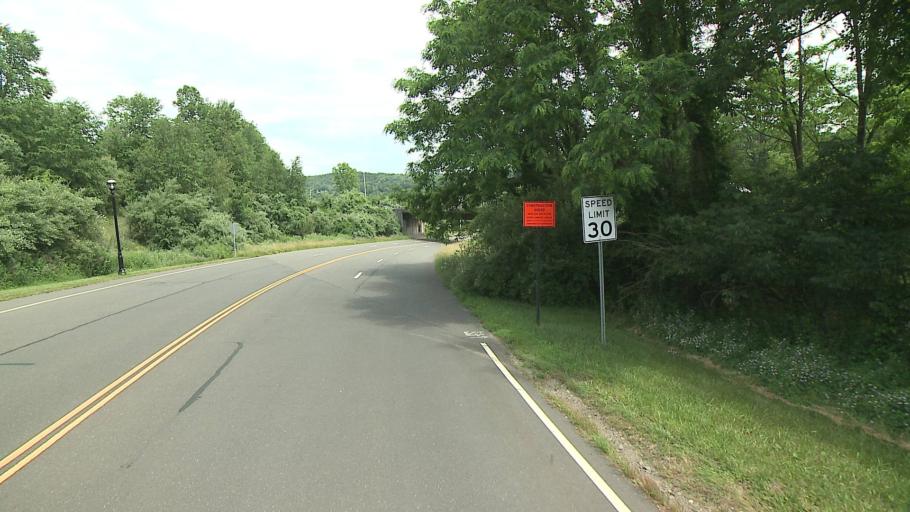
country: US
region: New York
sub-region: Putnam County
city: Peach Lake
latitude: 41.3890
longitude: -73.5232
